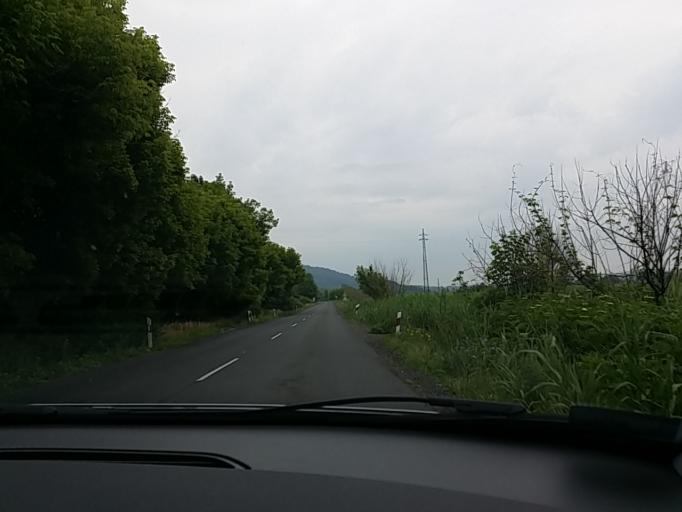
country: HU
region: Nograd
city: Batonyterenye
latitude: 47.9995
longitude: 19.8779
